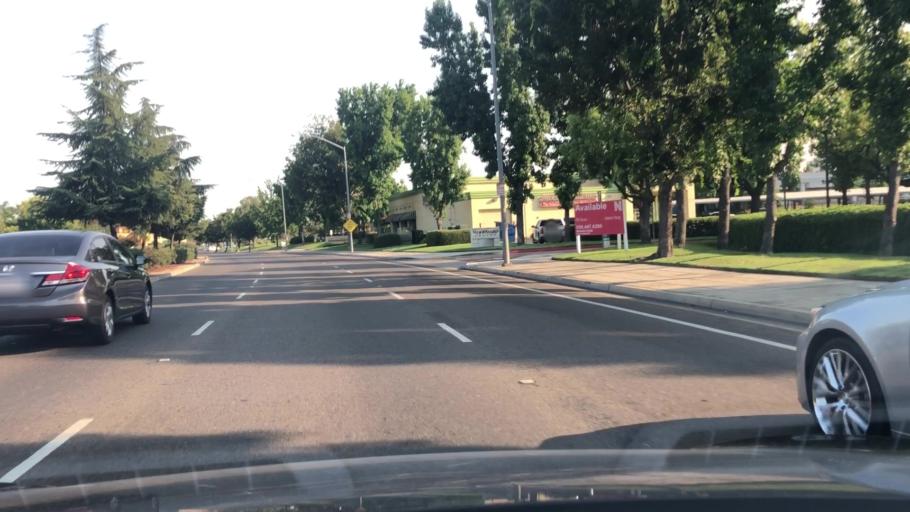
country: US
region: California
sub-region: Fresno County
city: Clovis
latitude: 36.8399
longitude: -119.7815
